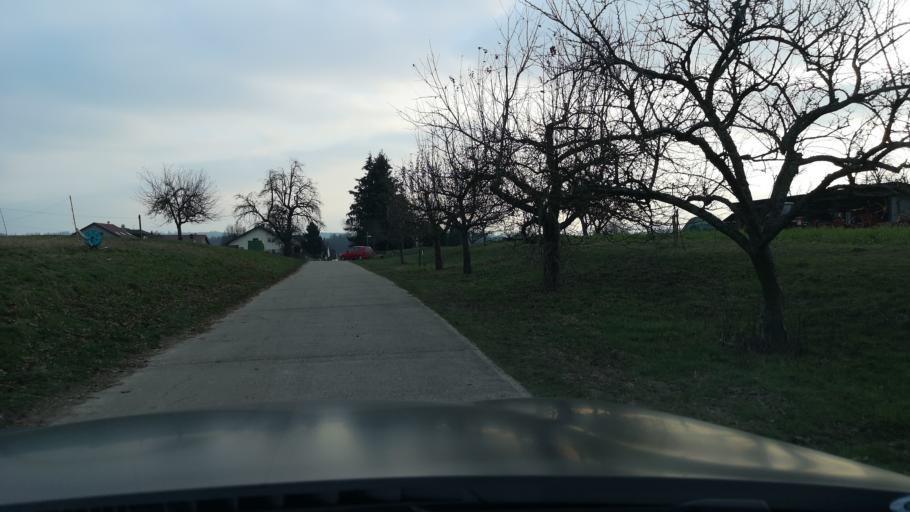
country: DE
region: Baden-Wuerttemberg
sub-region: Karlsruhe Region
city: Ettlingen
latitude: 48.9364
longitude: 8.4604
